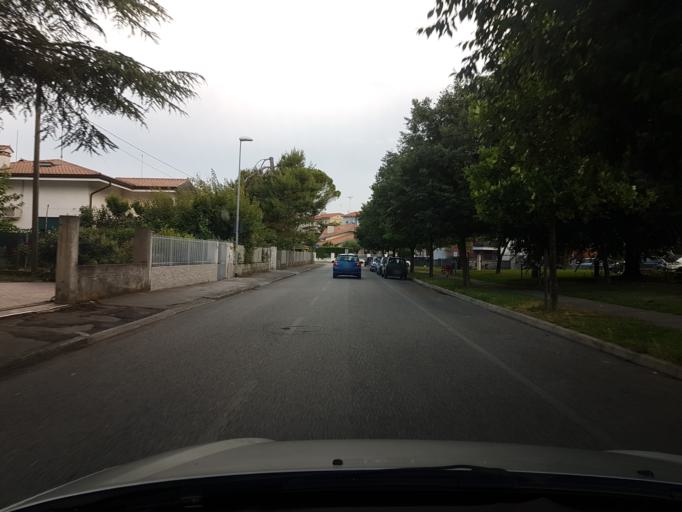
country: IT
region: Friuli Venezia Giulia
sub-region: Provincia di Gorizia
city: Ronchi dei Legionari
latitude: 45.8237
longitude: 13.5061
